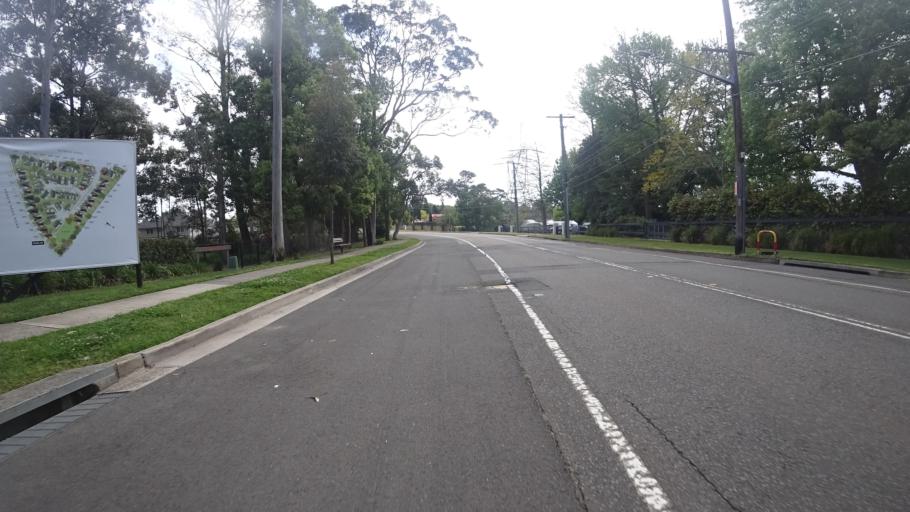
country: AU
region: New South Wales
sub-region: City of Sydney
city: North Turramurra
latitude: -33.6960
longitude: 151.1510
